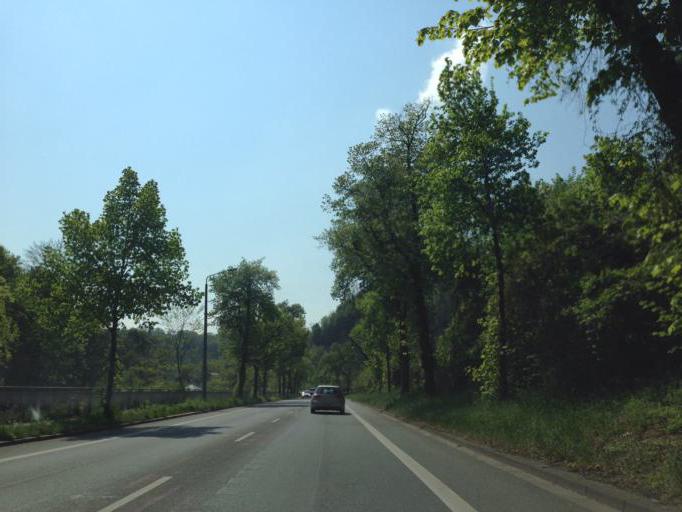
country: DE
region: Saxony
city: Bannewitz
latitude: 51.0280
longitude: 13.7001
